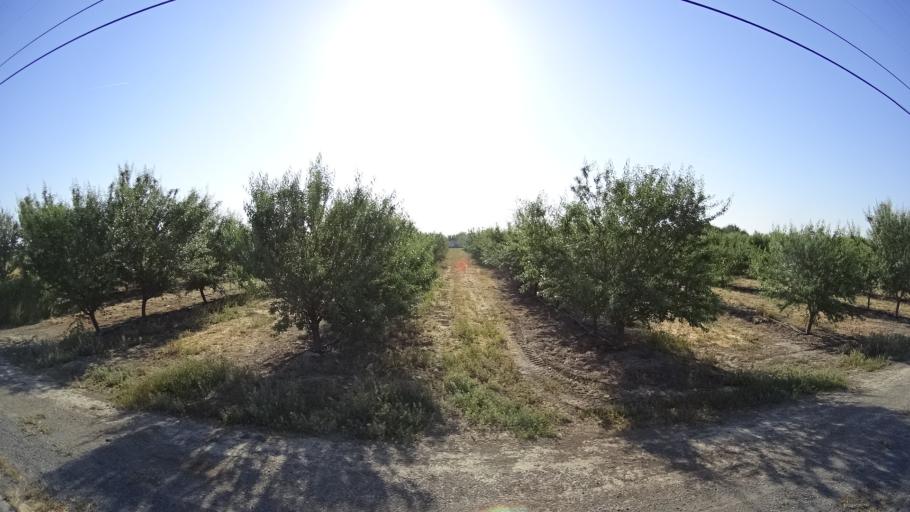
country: US
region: California
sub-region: Kings County
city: Armona
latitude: 36.2727
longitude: -119.7090
